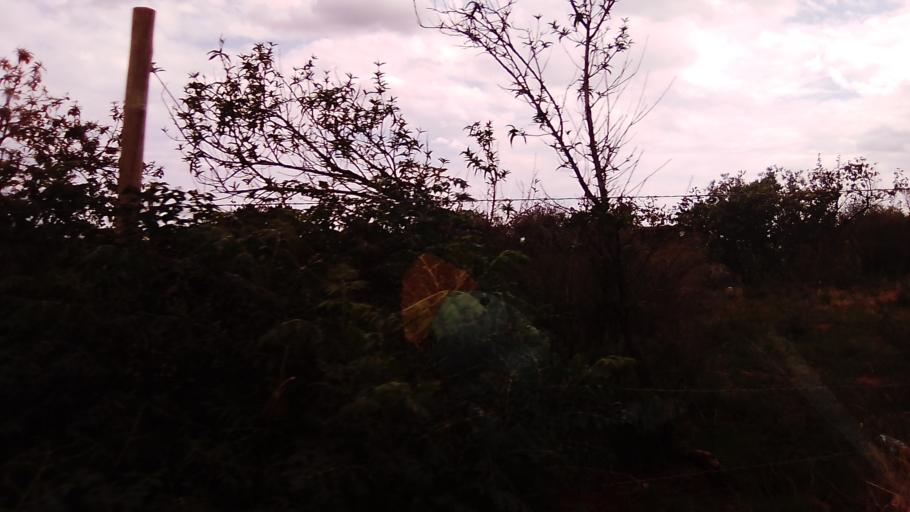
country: LS
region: Berea
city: Teyateyaneng
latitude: -29.3340
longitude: 27.7047
